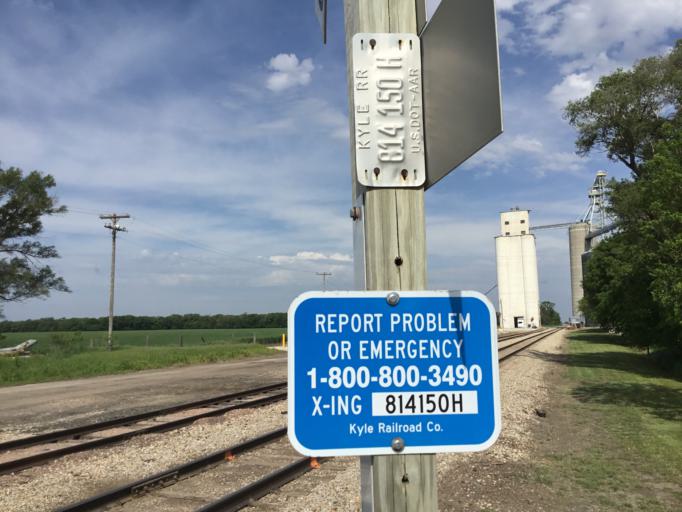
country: US
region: Kansas
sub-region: Mitchell County
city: Beloit
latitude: 39.4053
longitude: -97.9765
